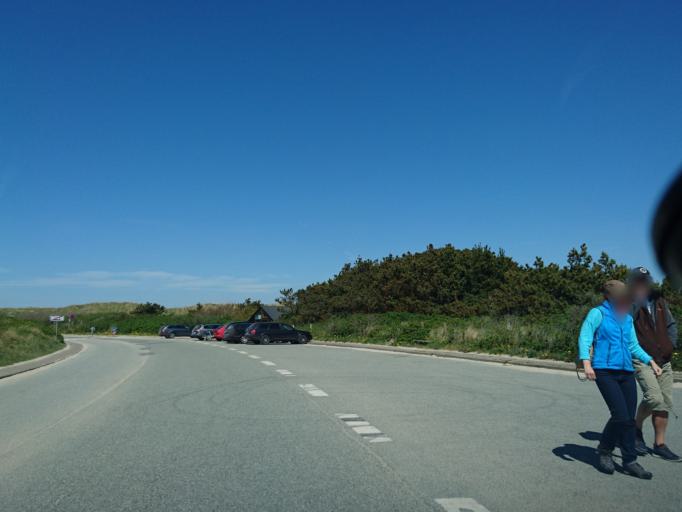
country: DK
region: North Denmark
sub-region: Hjorring Kommune
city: Sindal
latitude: 57.5943
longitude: 10.1846
